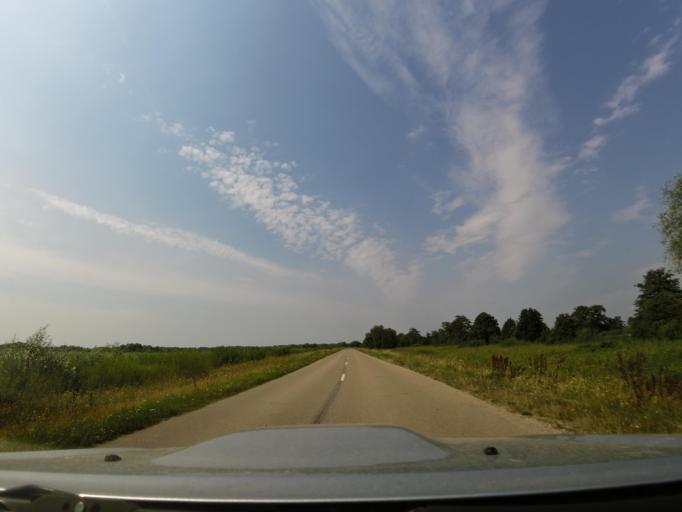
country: LT
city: Rusne
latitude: 55.3429
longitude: 21.3489
